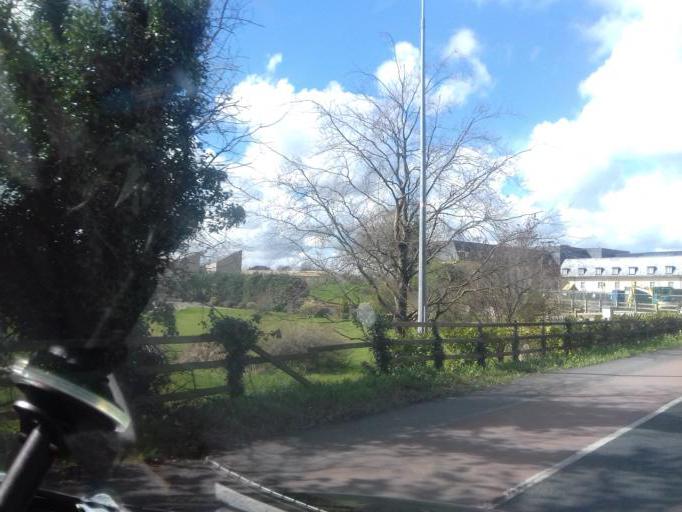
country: IE
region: Ulster
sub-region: An Cabhan
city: Cavan
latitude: 53.9836
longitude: -7.3390
